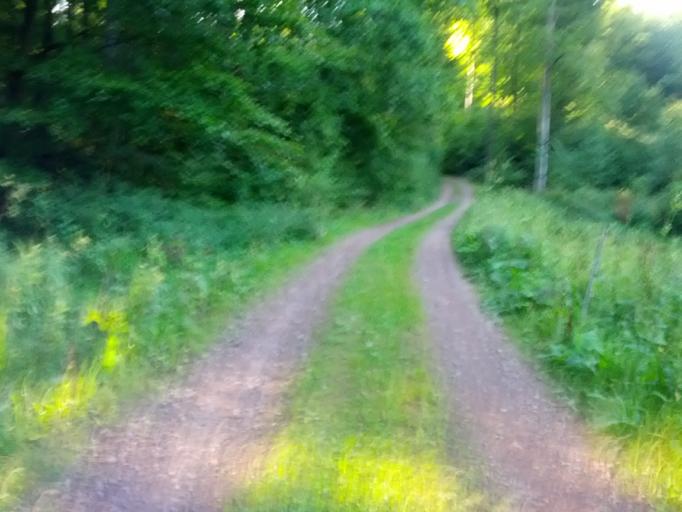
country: DE
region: Thuringia
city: Eisenach
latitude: 50.9430
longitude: 10.3407
